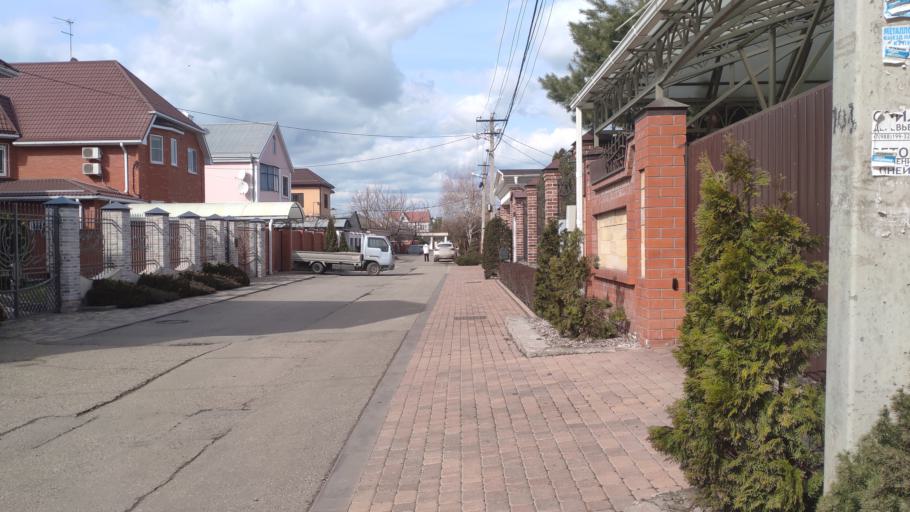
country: RU
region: Krasnodarskiy
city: Krasnodar
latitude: 45.0732
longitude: 39.0074
